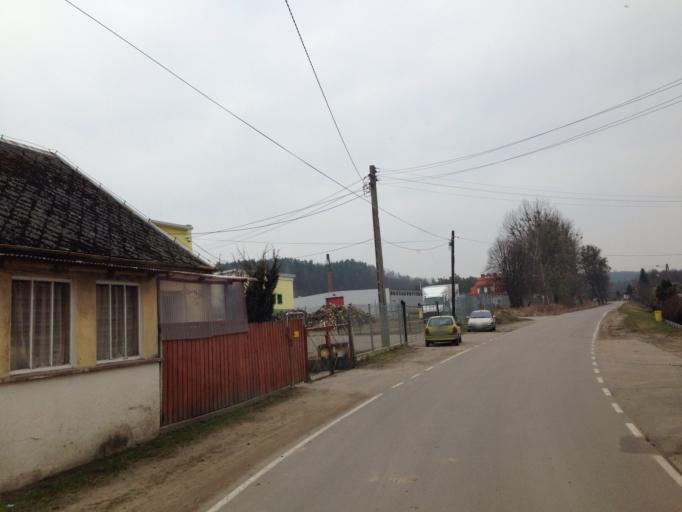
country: PL
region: Pomeranian Voivodeship
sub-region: Powiat kwidzynski
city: Sadlinki
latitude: 53.7408
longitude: 18.8170
